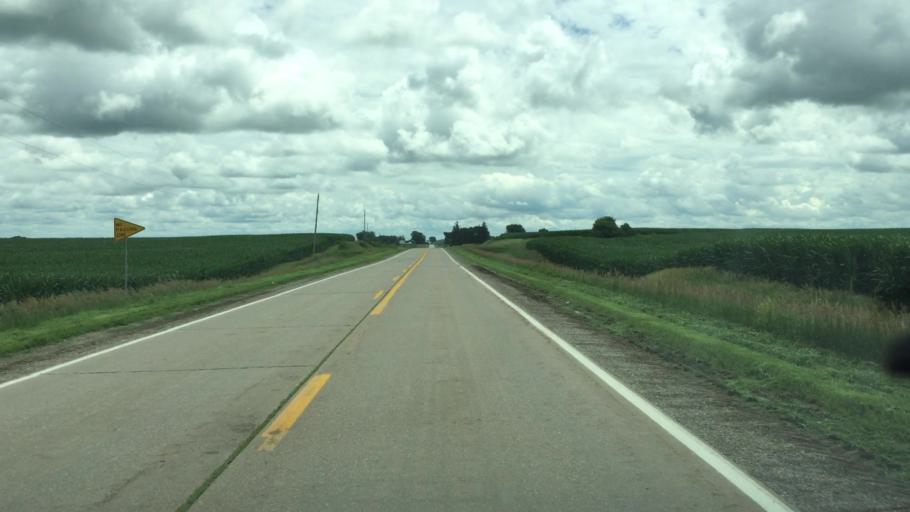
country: US
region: Iowa
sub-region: Jasper County
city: Monroe
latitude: 41.5807
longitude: -93.1285
